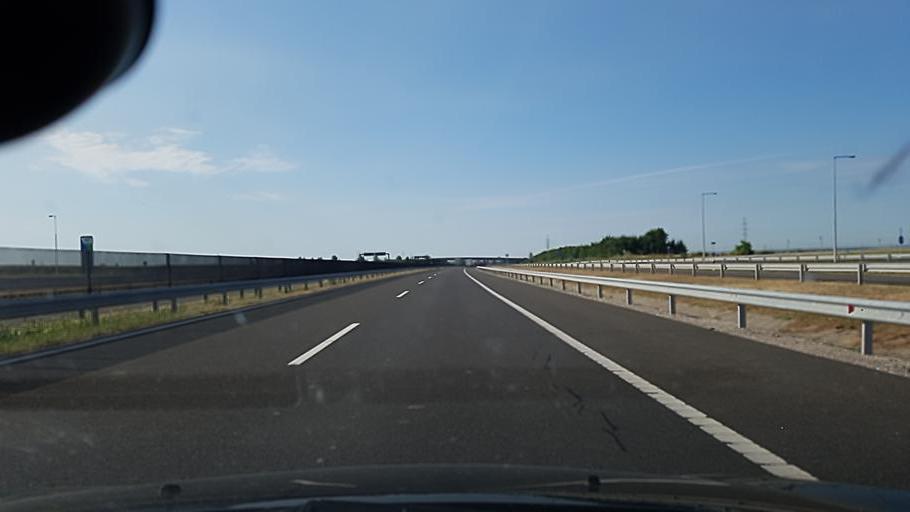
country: HU
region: Fejer
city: dunaujvaros
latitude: 46.9637
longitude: 18.8916
